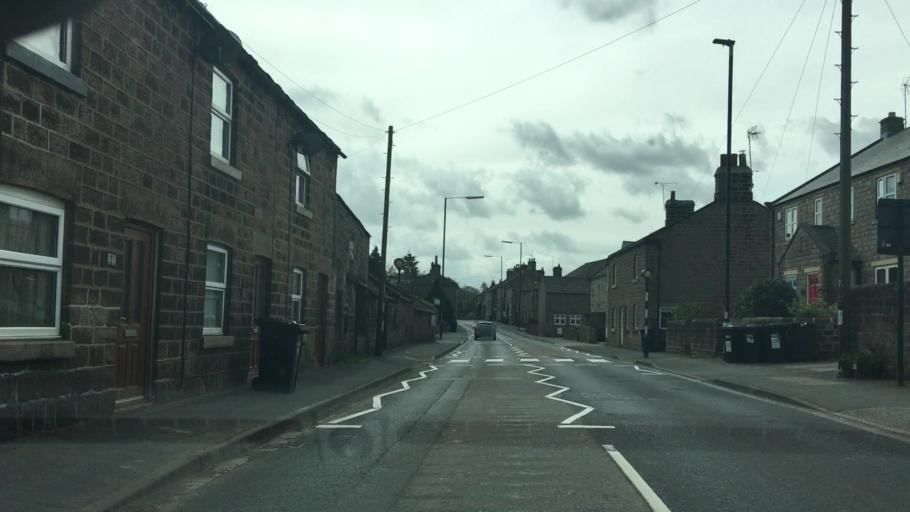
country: GB
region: England
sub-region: City and Borough of Leeds
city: Collingham
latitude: 53.9531
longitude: -1.4471
